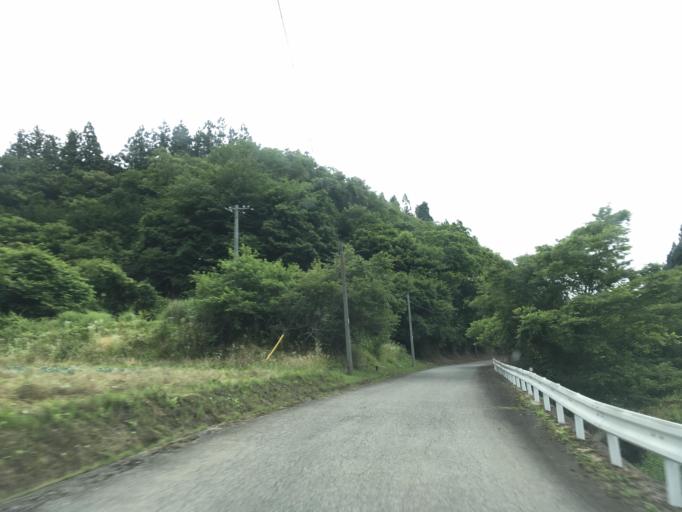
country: JP
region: Iwate
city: Ichinoseki
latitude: 38.8503
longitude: 141.3214
